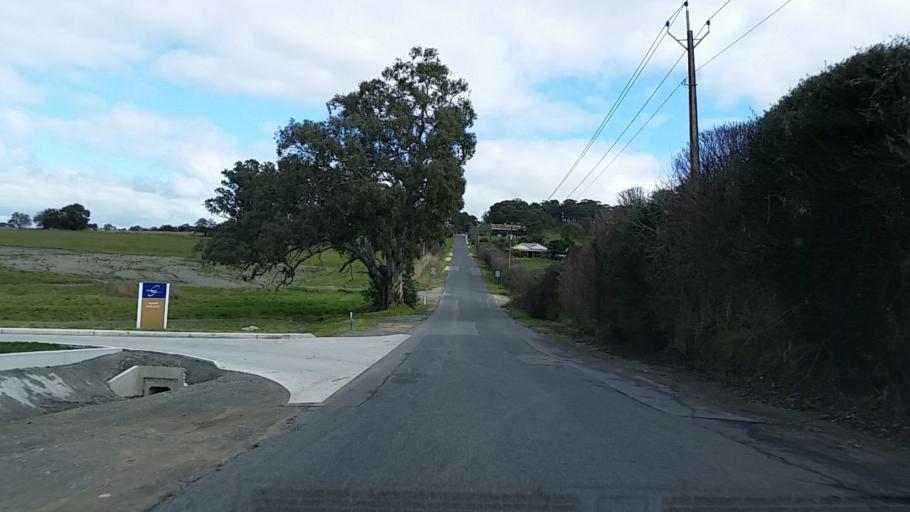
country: AU
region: South Australia
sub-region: Mount Barker
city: Little Hampton
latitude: -35.0657
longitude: 138.8499
